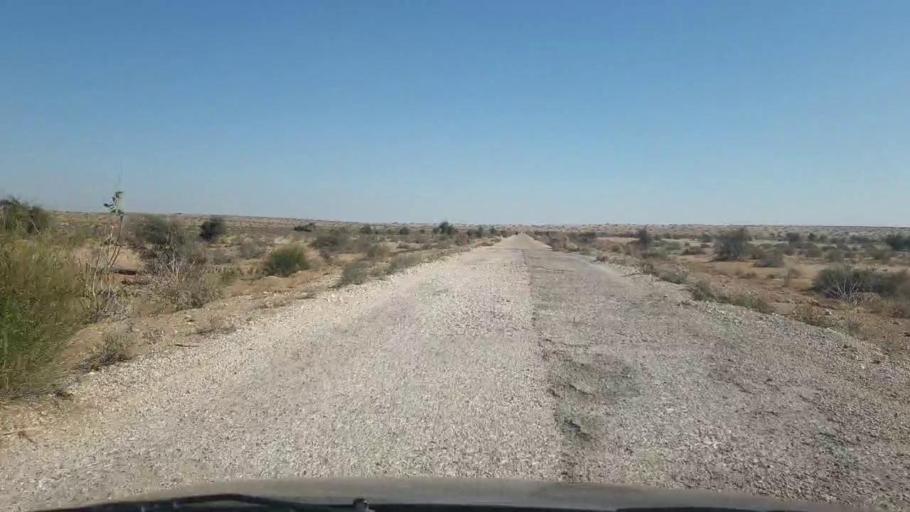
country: PK
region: Sindh
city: Bozdar
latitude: 27.0009
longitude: 68.8191
